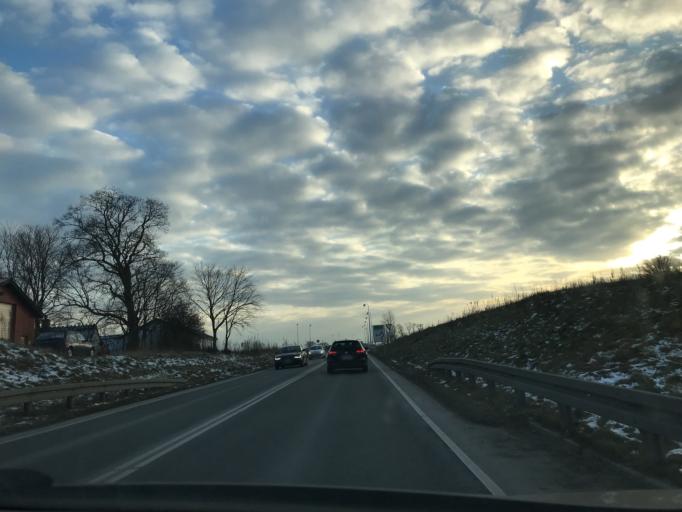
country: DK
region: Capital Region
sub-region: Egedal Kommune
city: Smorumnedre
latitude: 55.7206
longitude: 12.3142
